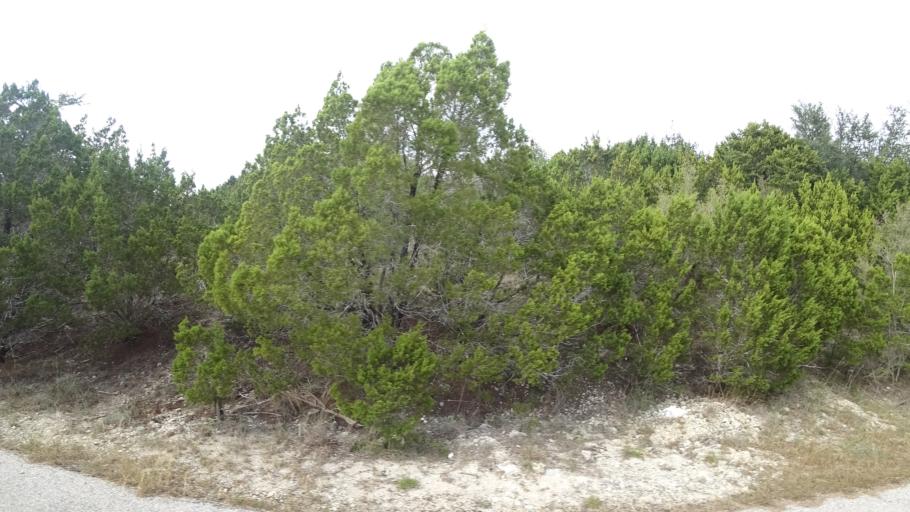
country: US
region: Texas
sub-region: Travis County
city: Hudson Bend
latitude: 30.3733
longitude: -97.9180
